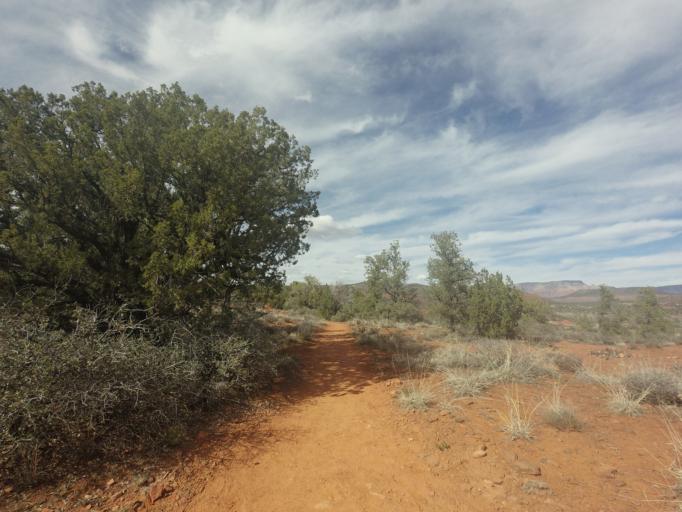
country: US
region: Arizona
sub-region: Yavapai County
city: West Sedona
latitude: 34.8062
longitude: -111.8319
